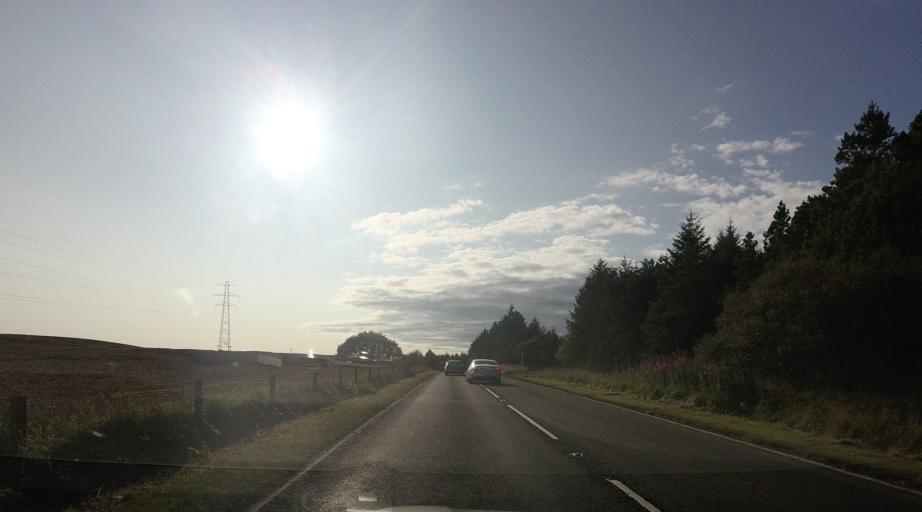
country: GB
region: Scotland
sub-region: Highland
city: Brora
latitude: 58.1671
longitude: -3.5485
